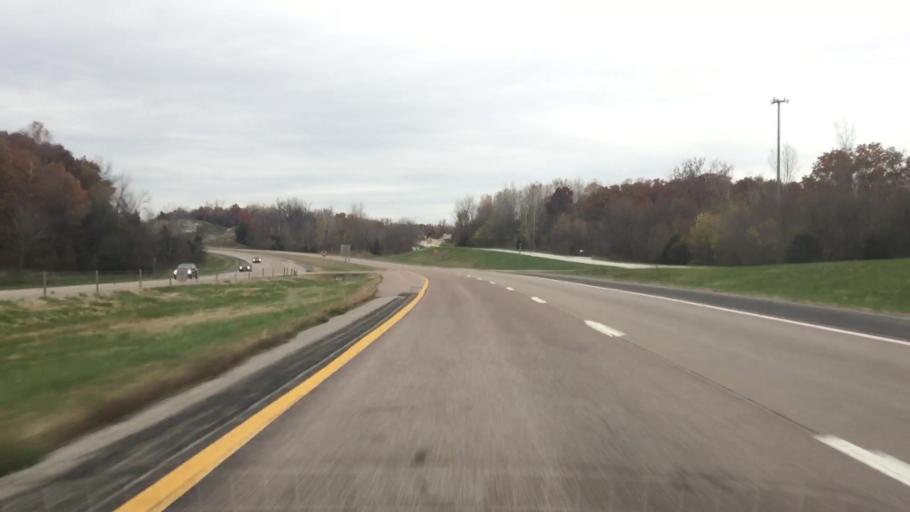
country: US
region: Missouri
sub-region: Cole County
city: Jefferson City
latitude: 38.6666
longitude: -92.2281
